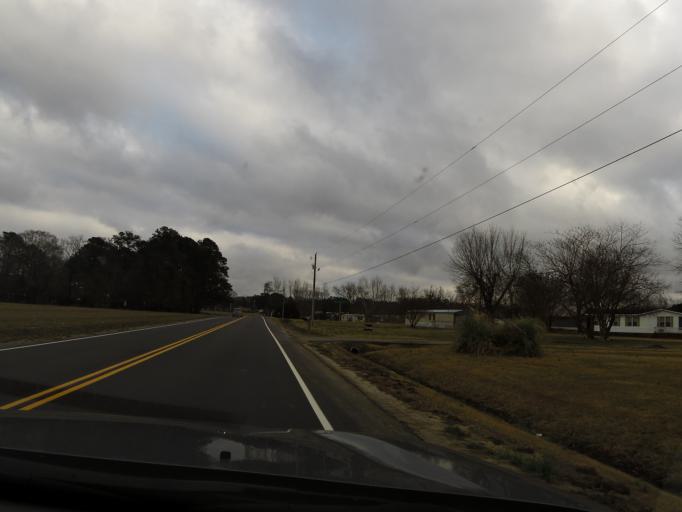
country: US
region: North Carolina
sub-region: Nash County
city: Rocky Mount
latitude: 35.8663
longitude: -77.7276
